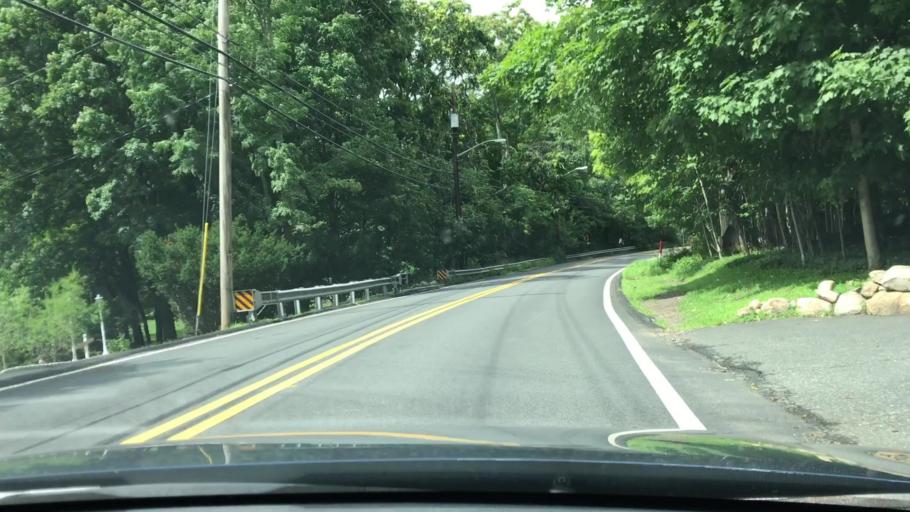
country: US
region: New Jersey
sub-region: Bergen County
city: Ramsey
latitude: 41.0419
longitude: -74.1628
